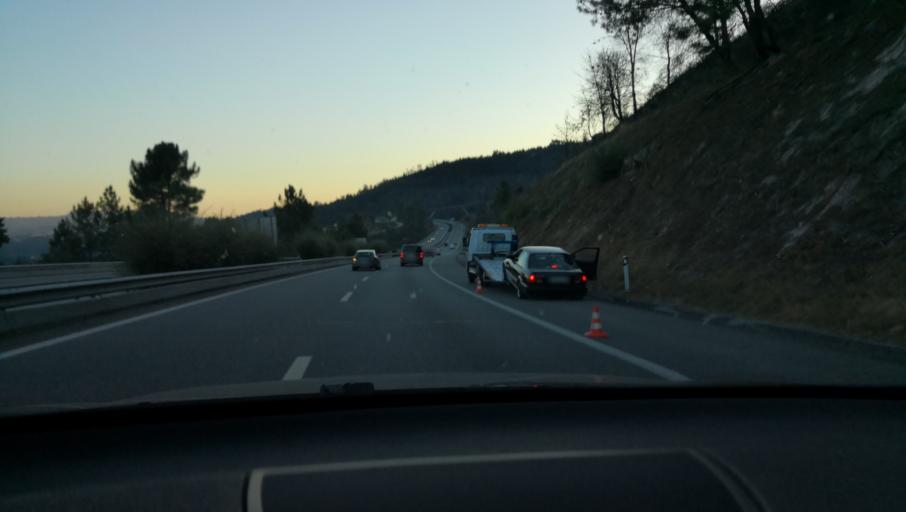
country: PT
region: Porto
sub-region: Amarante
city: Amarante
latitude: 41.2458
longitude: -8.1134
